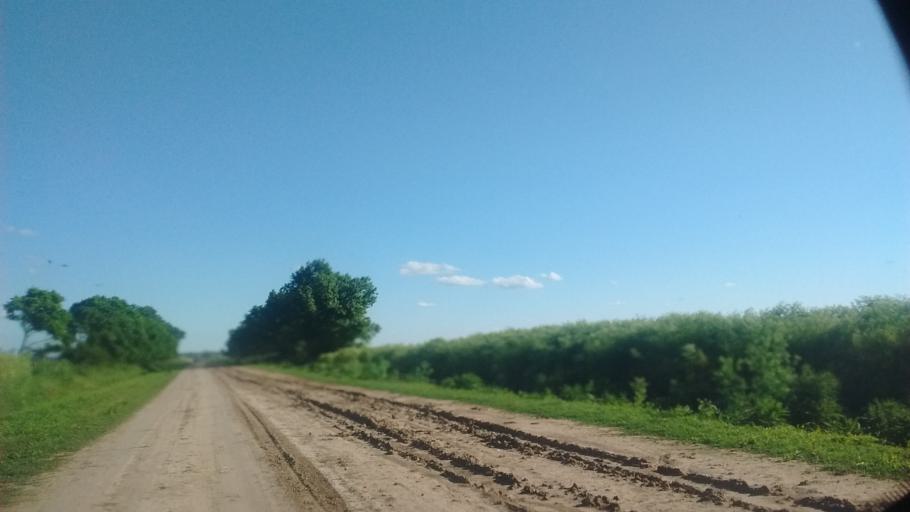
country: AR
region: Santa Fe
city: Funes
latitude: -32.8769
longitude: -60.7984
